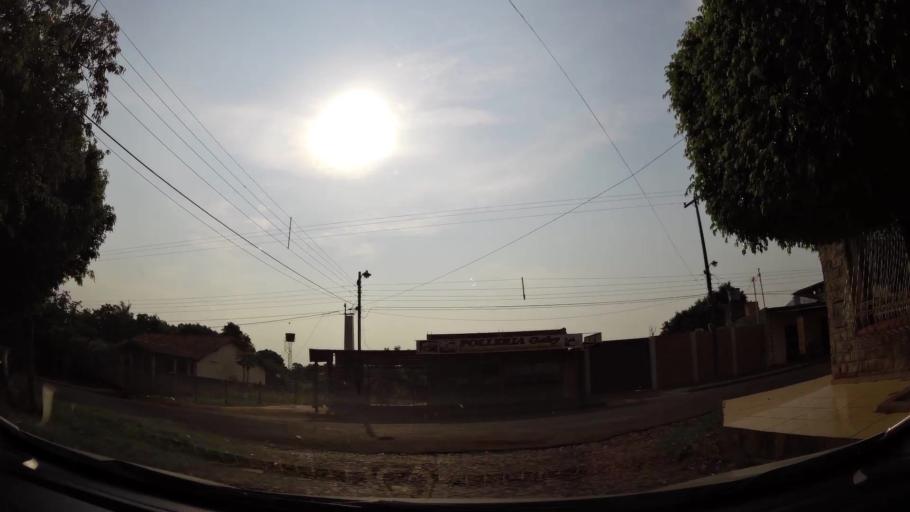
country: PY
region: Alto Parana
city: Ciudad del Este
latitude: -25.4859
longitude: -54.6549
